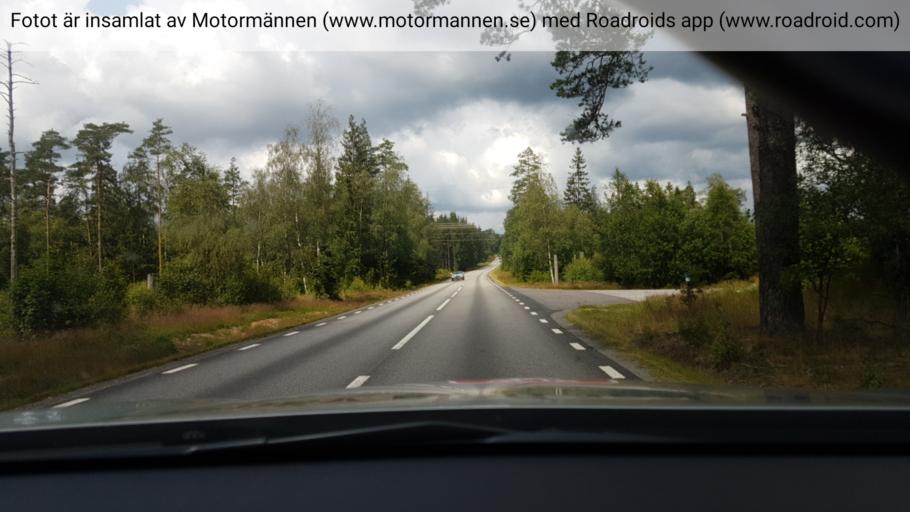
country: SE
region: Vaestra Goetaland
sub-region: Svenljunga Kommun
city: Svenljunga
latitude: 57.4682
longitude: 13.1701
